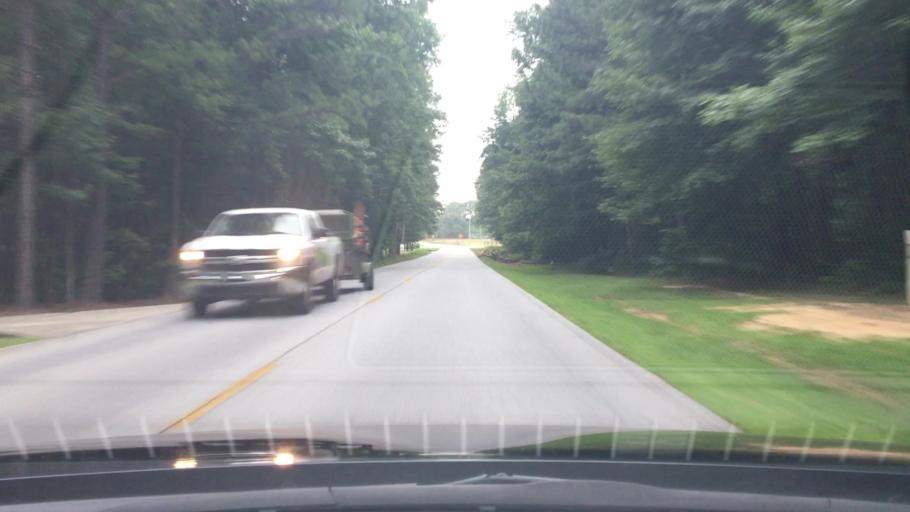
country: US
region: Georgia
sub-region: Coweta County
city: Senoia
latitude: 33.3072
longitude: -84.4688
